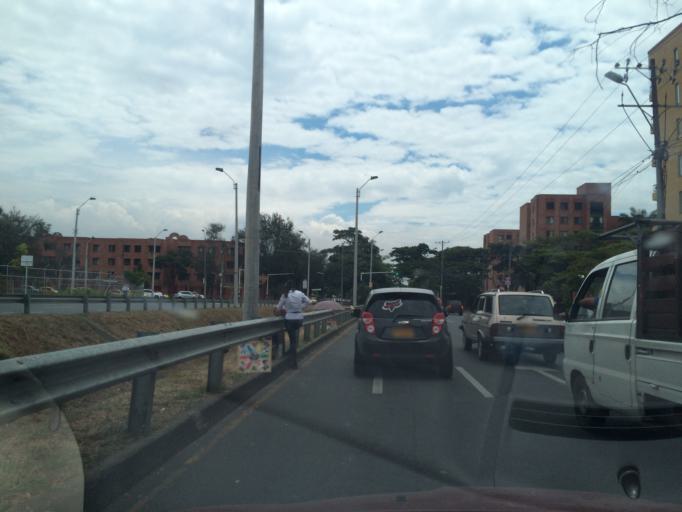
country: CO
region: Valle del Cauca
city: Cali
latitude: 3.3786
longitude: -76.5289
